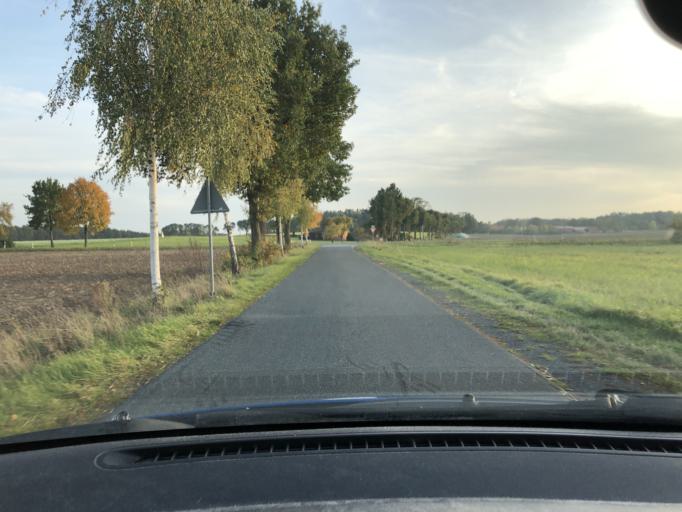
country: DE
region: Lower Saxony
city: Gohrde
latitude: 53.1304
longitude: 10.9461
